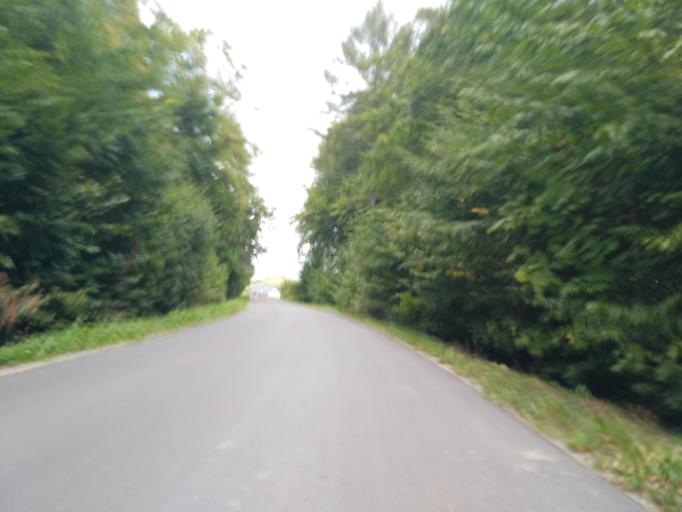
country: PL
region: Subcarpathian Voivodeship
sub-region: Powiat rzeszowski
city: Dynow
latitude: 49.7949
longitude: 22.2875
